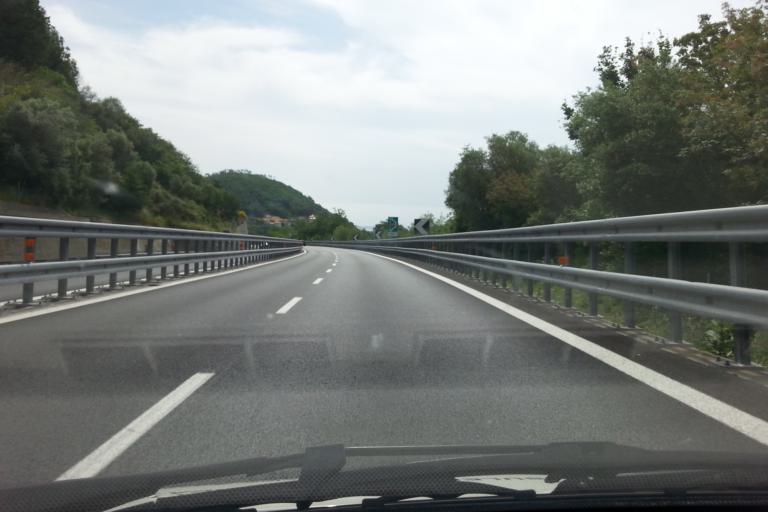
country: IT
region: Liguria
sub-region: Provincia di Savona
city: Vezzi Portio
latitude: 44.2266
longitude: 8.3757
